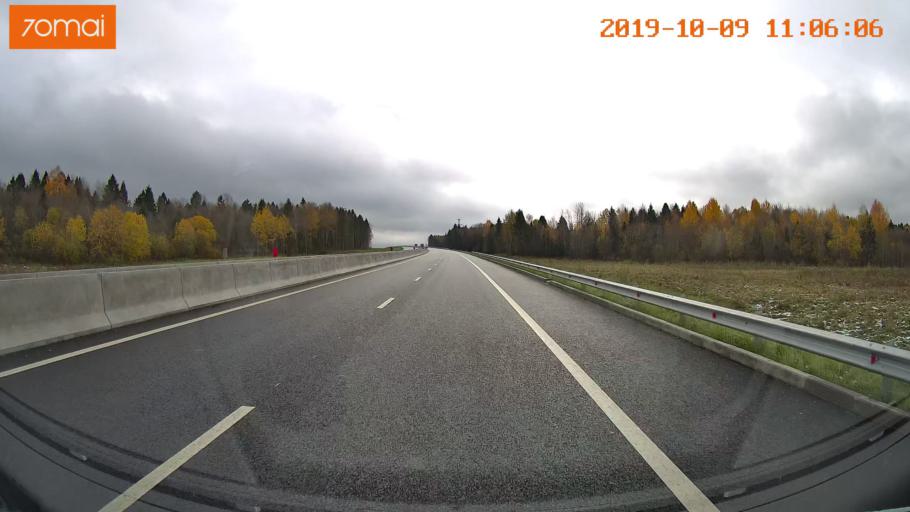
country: RU
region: Vologda
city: Molochnoye
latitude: 59.1910
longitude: 39.7584
